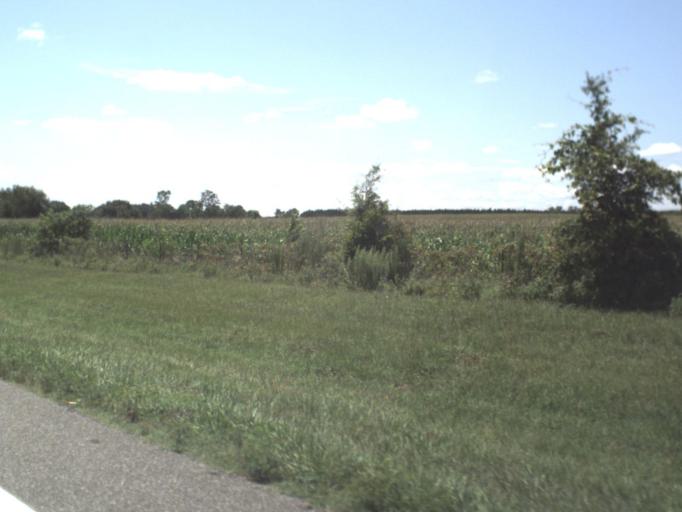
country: US
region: Florida
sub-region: Lafayette County
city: Mayo
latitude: 30.0534
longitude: -83.1014
